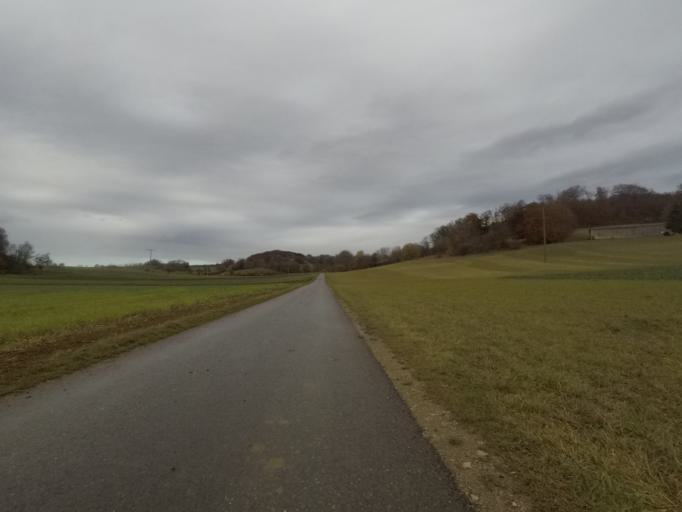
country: DE
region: Baden-Wuerttemberg
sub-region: Tuebingen Region
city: Sankt Johann
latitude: 48.4231
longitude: 9.2881
